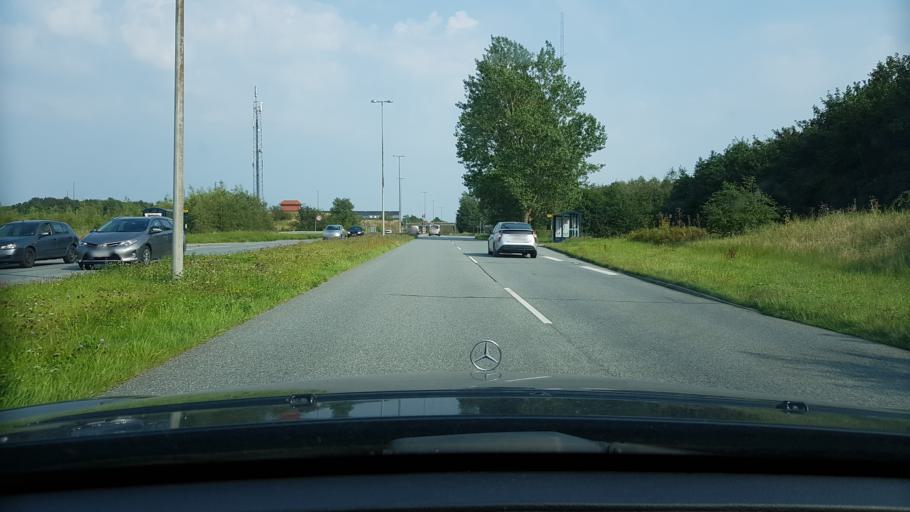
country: DK
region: North Denmark
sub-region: Alborg Kommune
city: Gistrup
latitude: 57.0300
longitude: 9.9862
